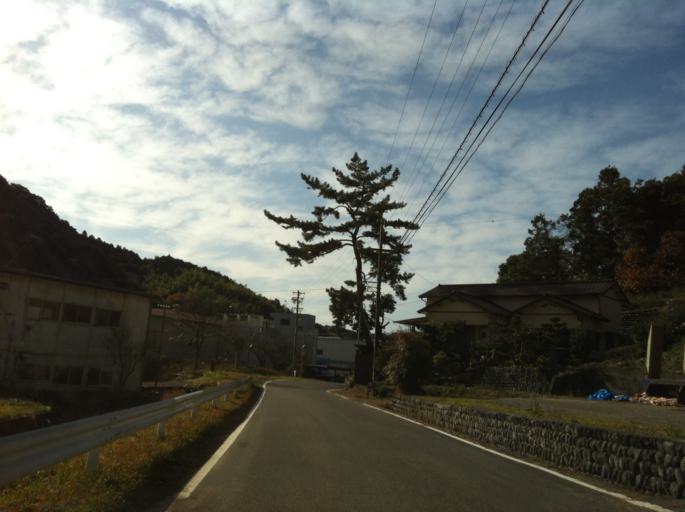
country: JP
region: Shizuoka
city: Yaizu
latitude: 34.9250
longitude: 138.2975
